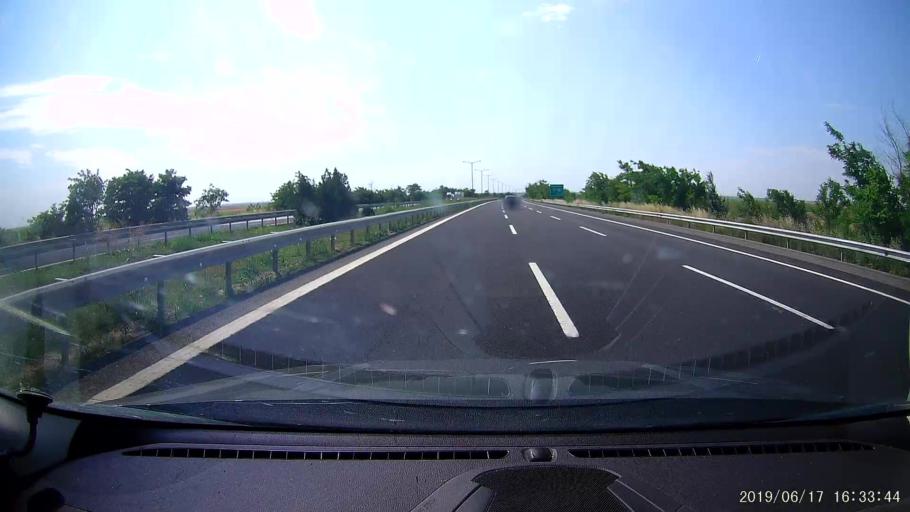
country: TR
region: Kirklareli
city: Buyukkaristiran
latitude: 41.3838
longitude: 27.5638
